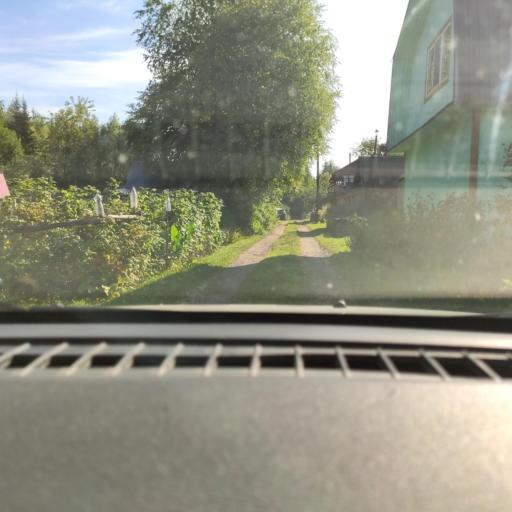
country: RU
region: Perm
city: Novyye Lyady
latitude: 58.0613
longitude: 56.5809
